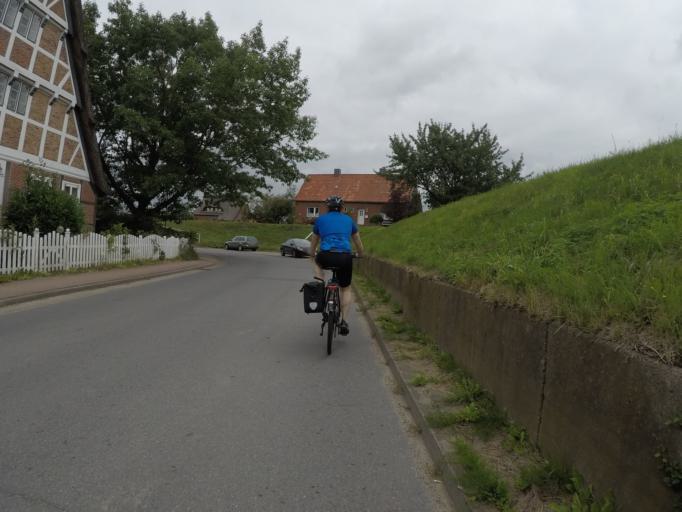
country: DE
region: Lower Saxony
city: Guderhandviertel
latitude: 53.5565
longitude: 9.6057
